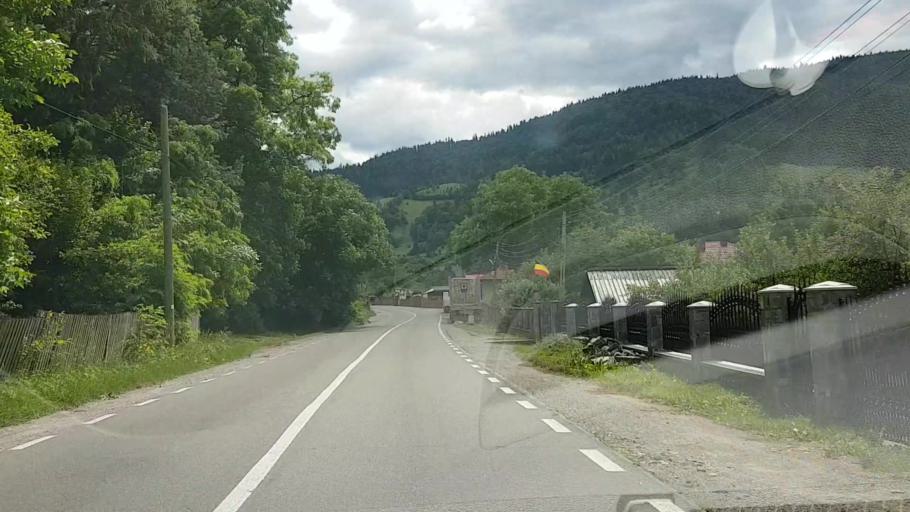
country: RO
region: Neamt
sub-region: Comuna Poiana Teiului
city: Poiana Teiului
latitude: 47.1253
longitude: 25.9069
